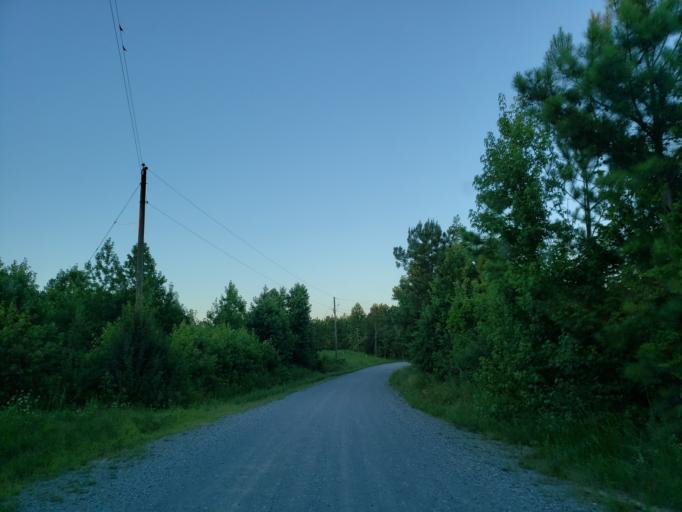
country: US
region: Georgia
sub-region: Bartow County
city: Cartersville
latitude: 34.0598
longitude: -84.8512
